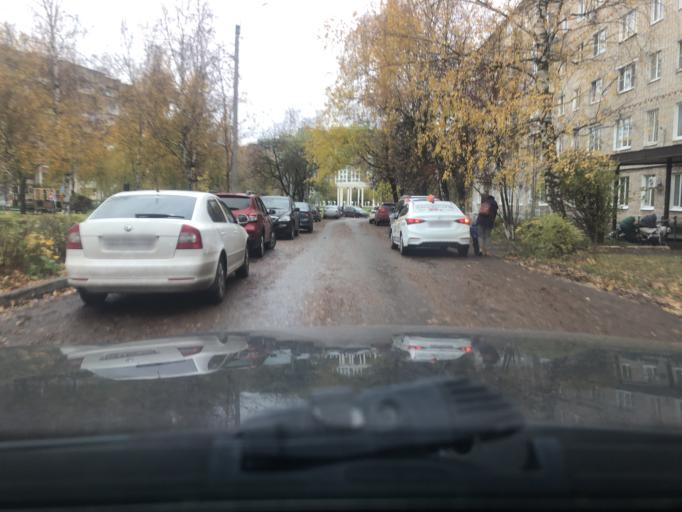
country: RU
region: Moskovskaya
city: Sergiyev Posad
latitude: 56.3197
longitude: 38.1361
